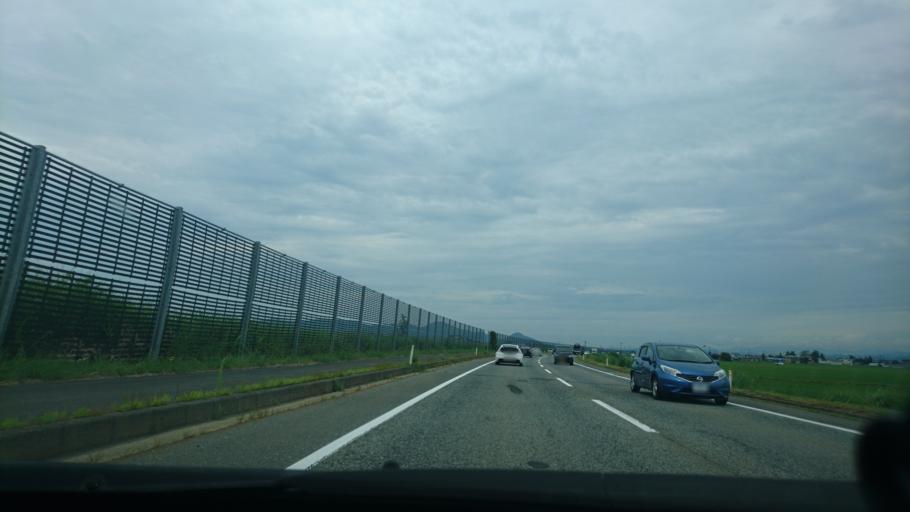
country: JP
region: Akita
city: Omagari
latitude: 39.4234
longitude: 140.5174
